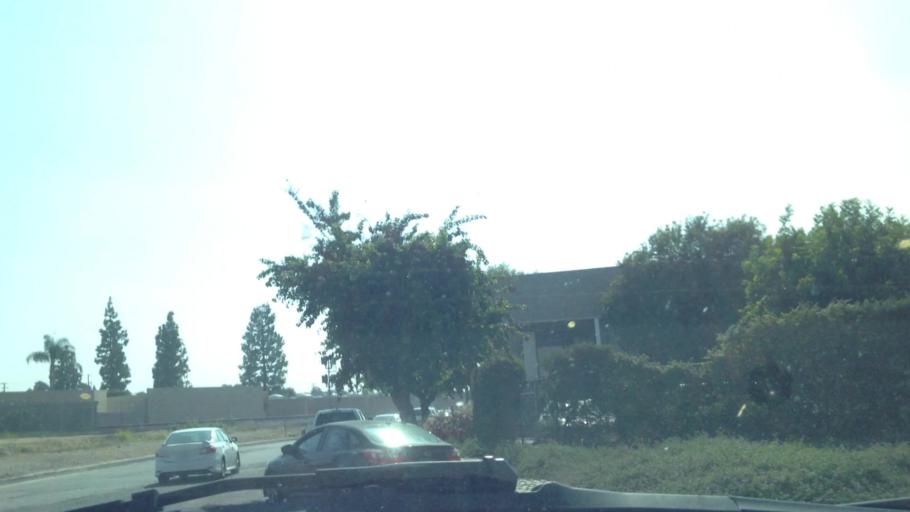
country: US
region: California
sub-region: Orange County
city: Buena Park
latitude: 33.8725
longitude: -117.9645
